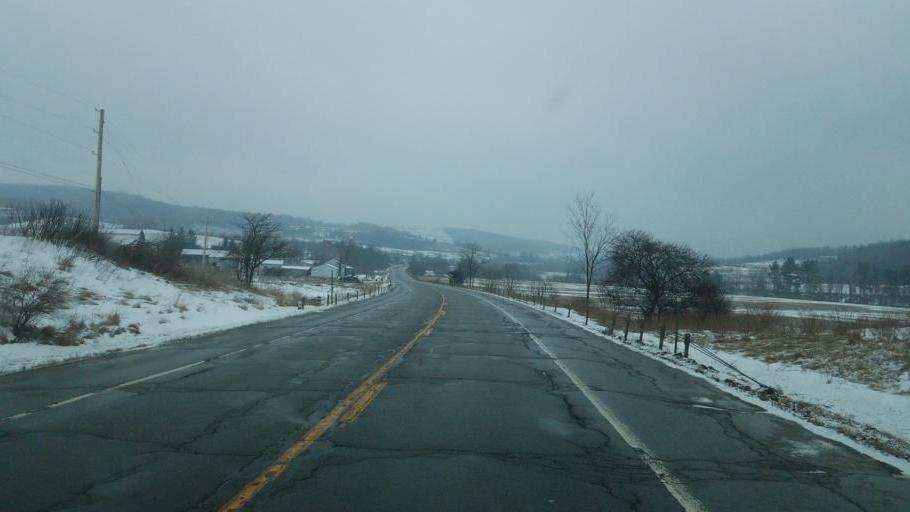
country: US
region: Pennsylvania
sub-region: Tioga County
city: Elkland
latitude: 42.0974
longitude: -77.4410
